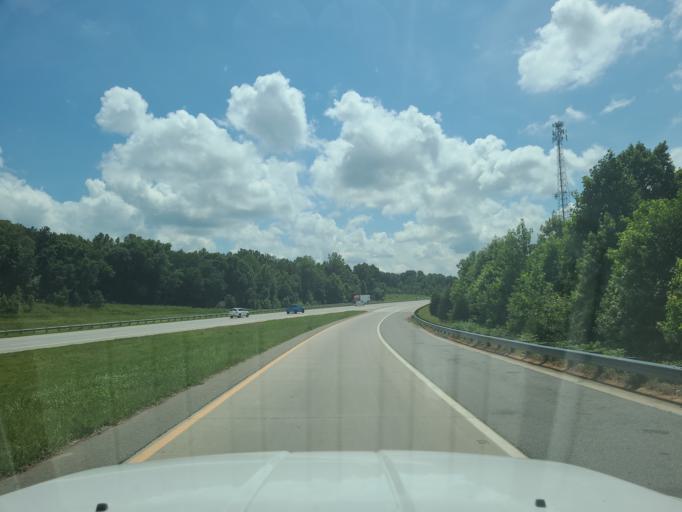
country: US
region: North Carolina
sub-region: Rowan County
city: East Spencer
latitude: 35.6782
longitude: -80.4159
